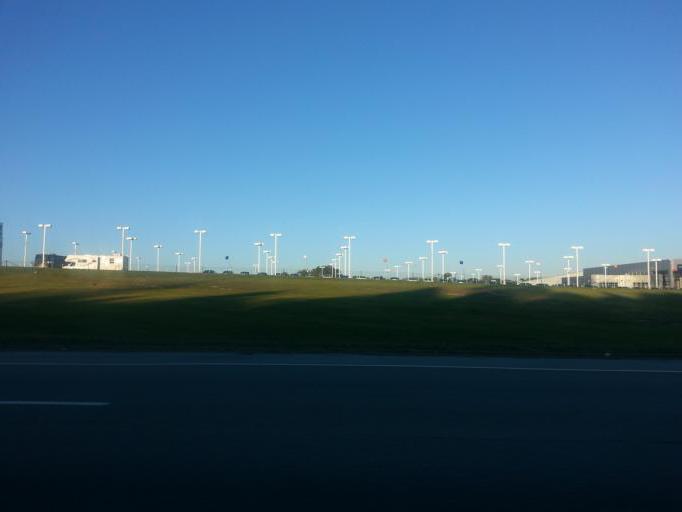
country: US
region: Tennessee
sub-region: Anderson County
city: Norris
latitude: 36.1704
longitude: -84.0848
